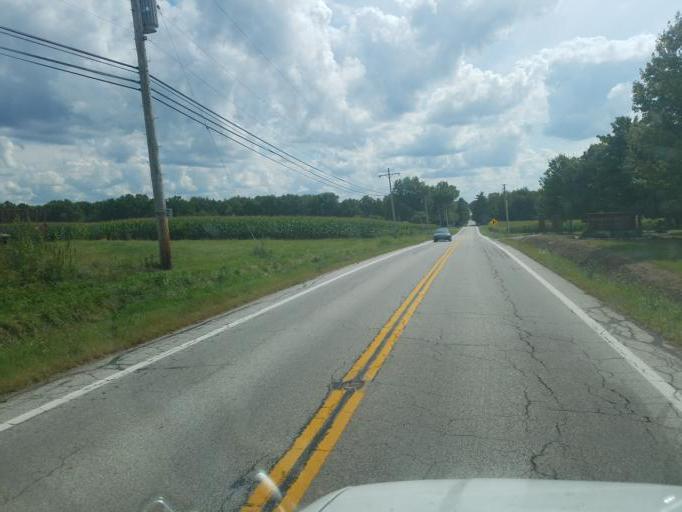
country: US
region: Ohio
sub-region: Portage County
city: Hiram
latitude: 41.3765
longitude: -81.1431
